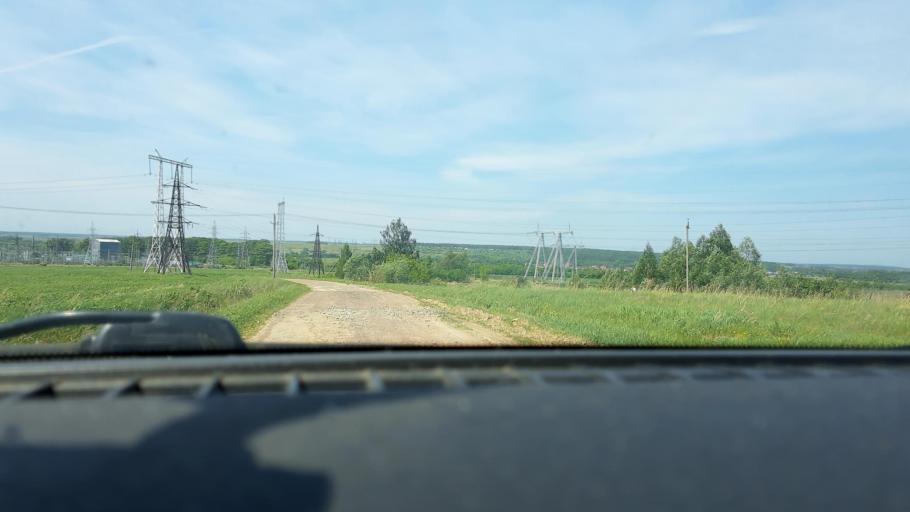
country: RU
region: Bashkortostan
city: Avdon
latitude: 54.4292
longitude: 55.8383
